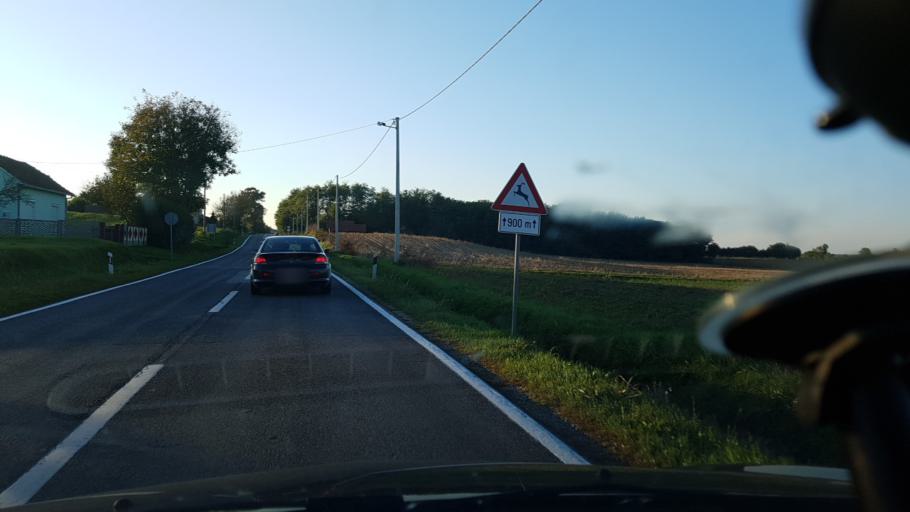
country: HR
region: Koprivnicko-Krizevacka
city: Hlebine
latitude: 46.1090
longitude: 16.9009
